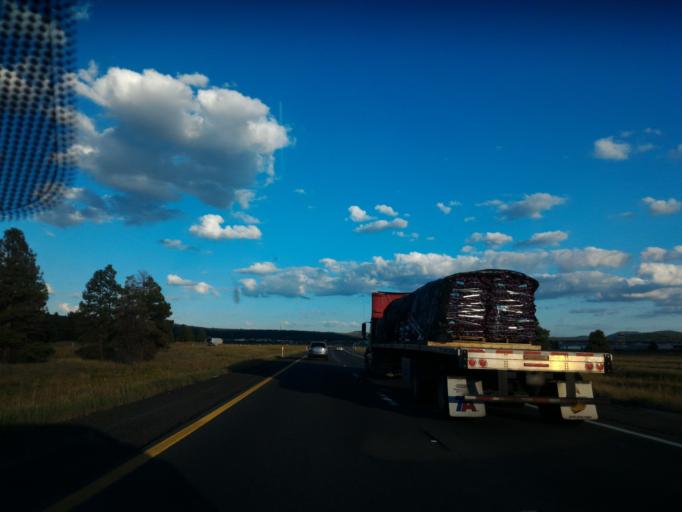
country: US
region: Arizona
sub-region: Coconino County
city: Parks
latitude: 35.2441
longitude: -111.8404
